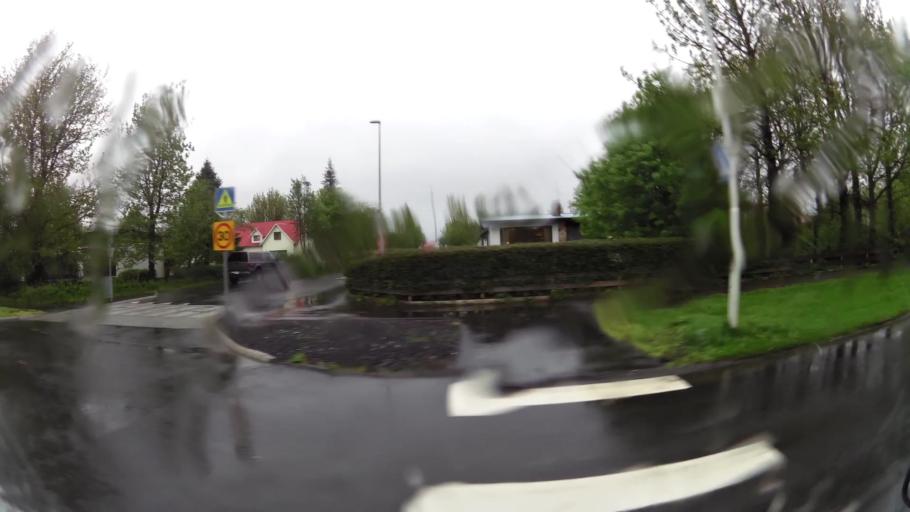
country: IS
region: South
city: Selfoss
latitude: 63.9326
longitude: -21.0077
